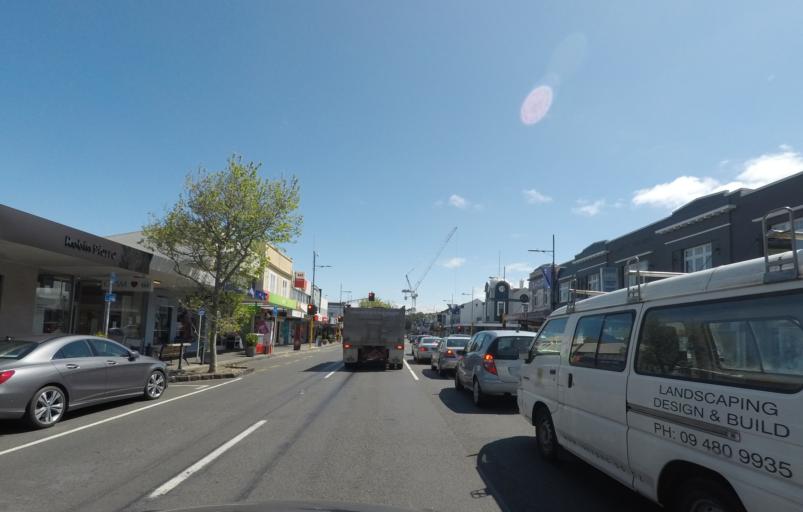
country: NZ
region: Auckland
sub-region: Auckland
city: Auckland
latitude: -36.8808
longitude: 174.7988
